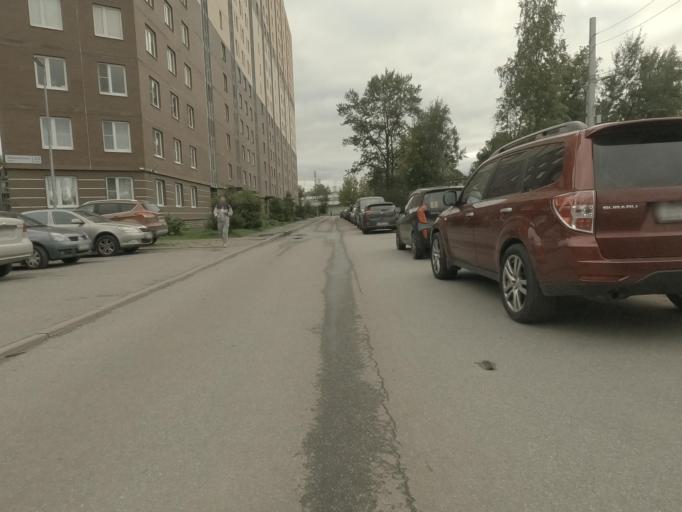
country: RU
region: St.-Petersburg
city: Krasnogvargeisky
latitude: 59.9796
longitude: 30.5100
